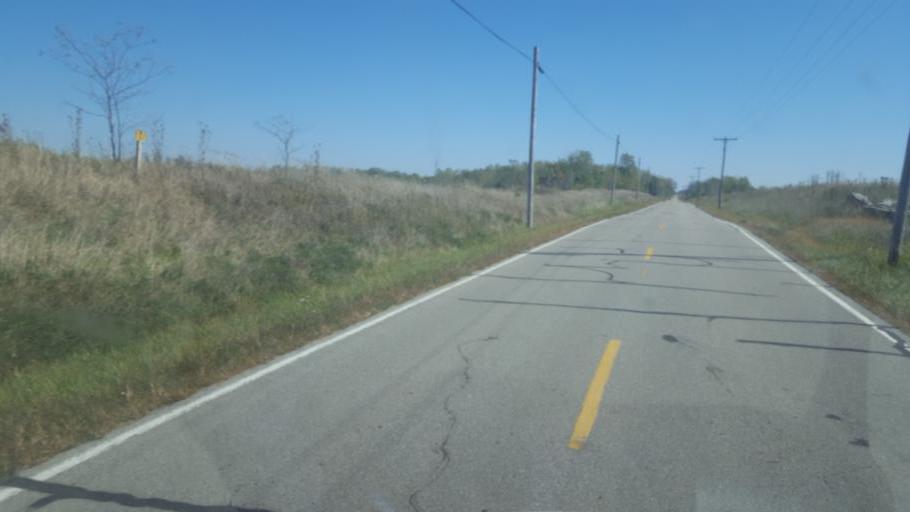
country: US
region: Ohio
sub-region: Crawford County
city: Bucyrus
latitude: 40.8630
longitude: -83.0681
